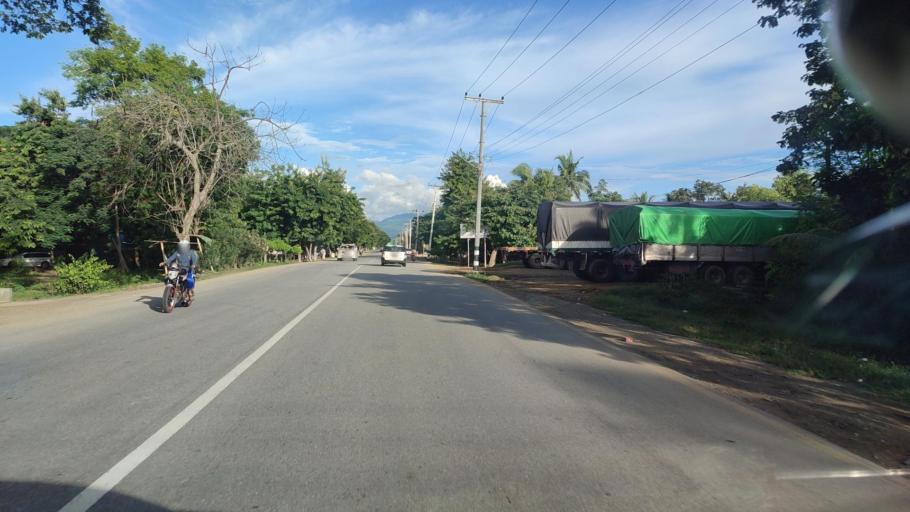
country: MM
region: Mandalay
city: Yamethin
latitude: 20.1221
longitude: 96.2120
